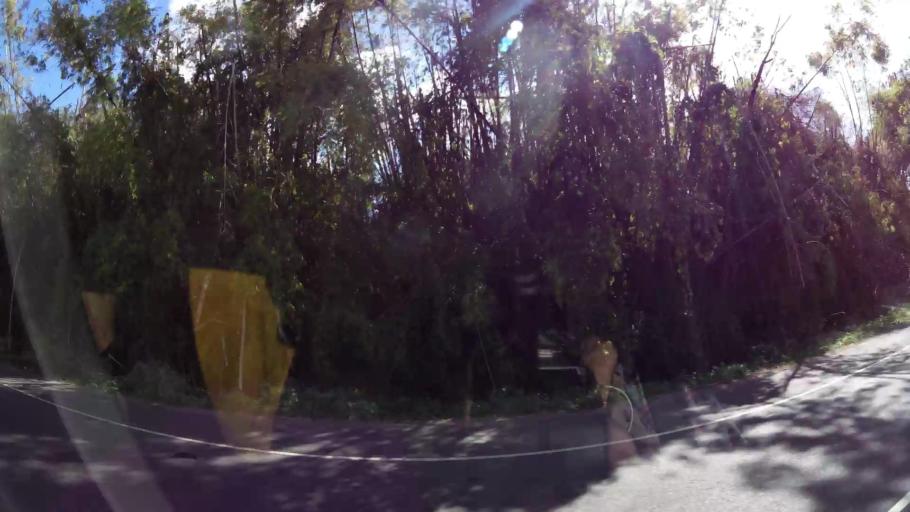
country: DO
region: Santo Domingo
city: Santo Domingo Oeste
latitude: 18.5603
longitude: -70.0607
